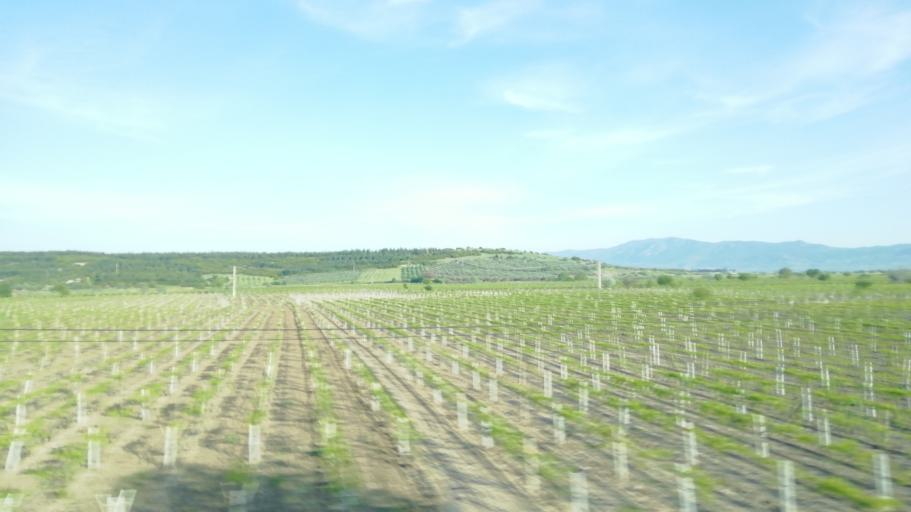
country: TR
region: Manisa
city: Halitpasa
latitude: 38.7810
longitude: 27.6684
